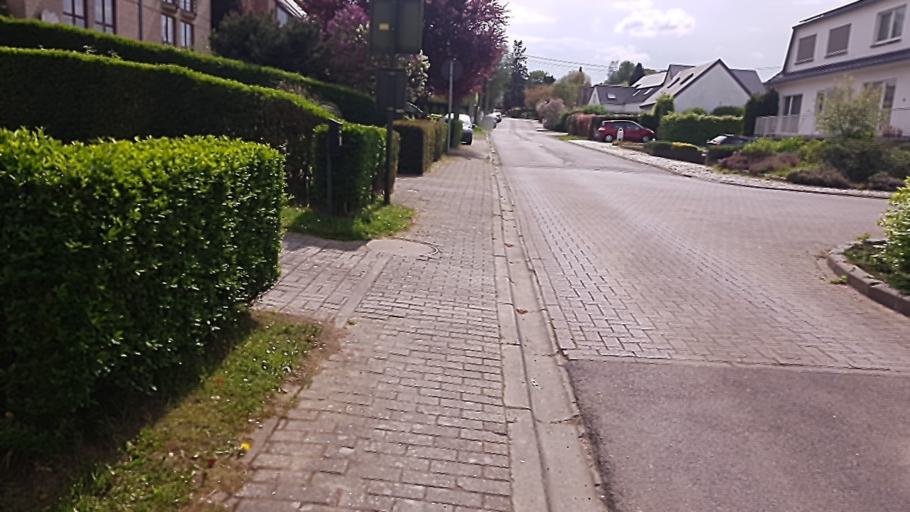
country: BE
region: Wallonia
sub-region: Province du Brabant Wallon
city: Wavre
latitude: 50.7134
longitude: 4.6282
